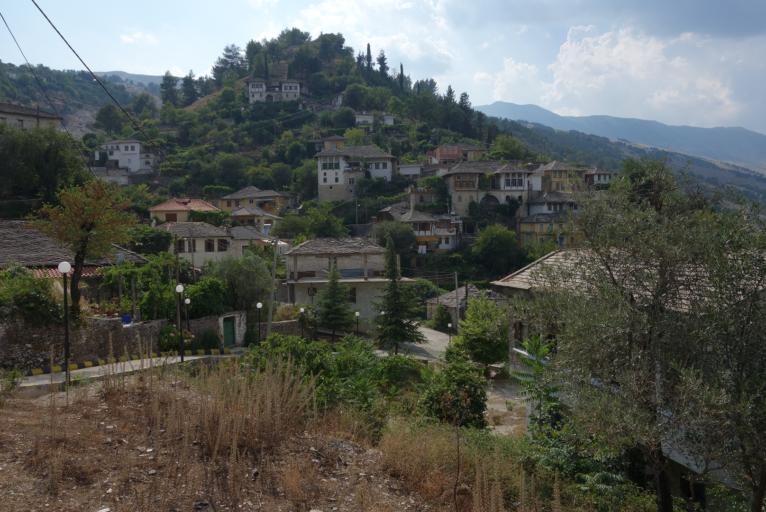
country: AL
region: Gjirokaster
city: Gjirokaster
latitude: 40.0727
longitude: 20.1378
